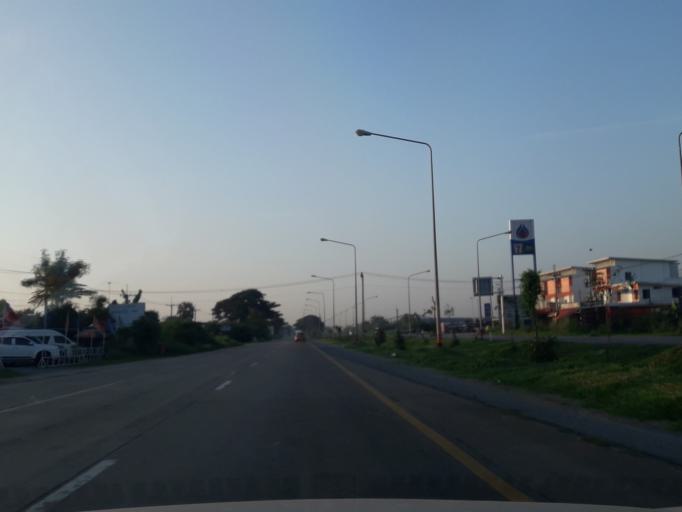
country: TH
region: Phra Nakhon Si Ayutthaya
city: Bang Ban
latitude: 14.3619
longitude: 100.5287
